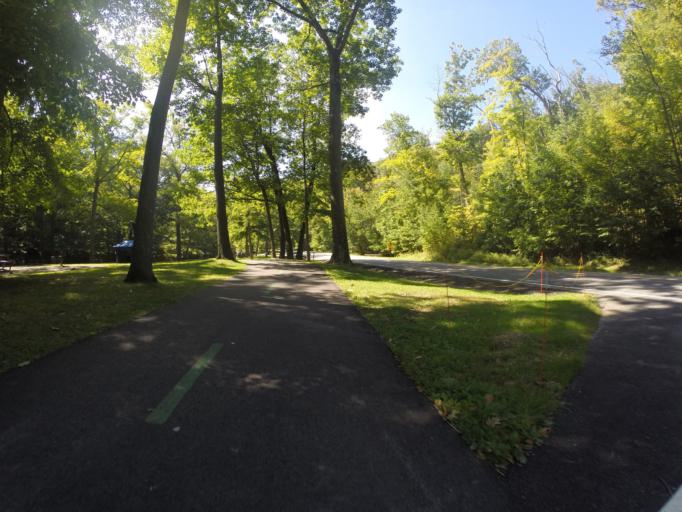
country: US
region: Ohio
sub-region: Cuyahoga County
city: Richmond Heights
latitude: 41.5610
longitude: -81.5332
